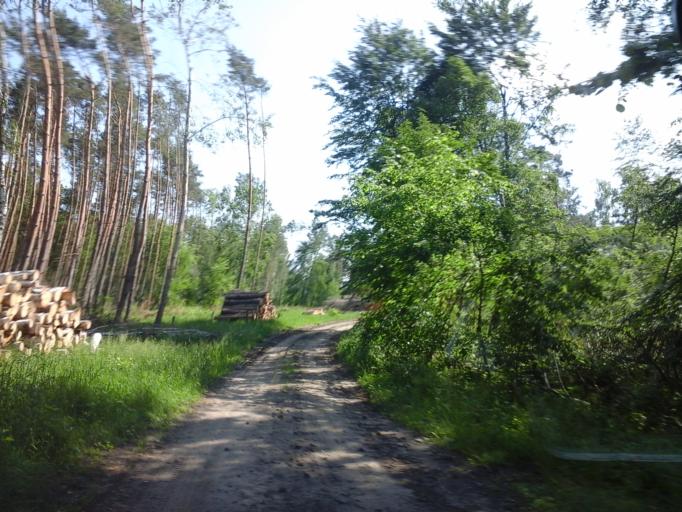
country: PL
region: West Pomeranian Voivodeship
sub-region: Powiat choszczenski
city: Bierzwnik
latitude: 53.0094
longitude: 15.6937
